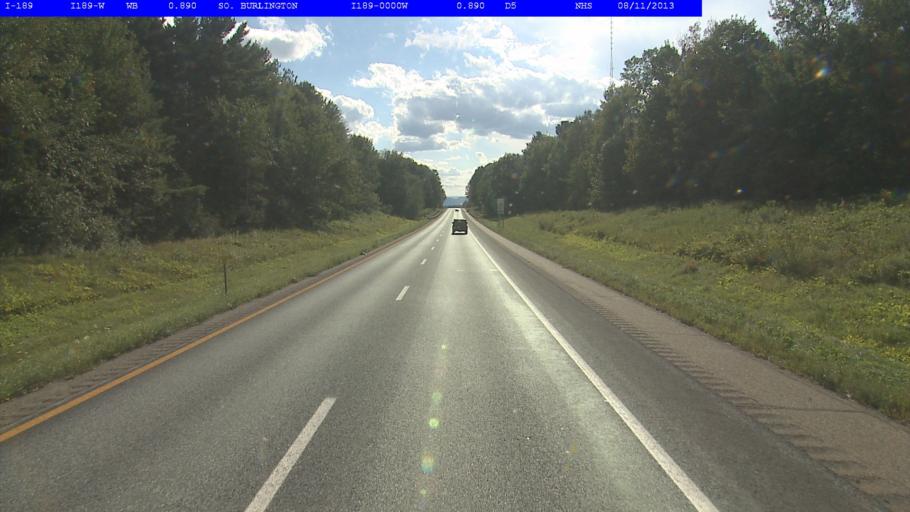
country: US
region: Vermont
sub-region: Chittenden County
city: South Burlington
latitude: 44.4510
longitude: -73.1926
